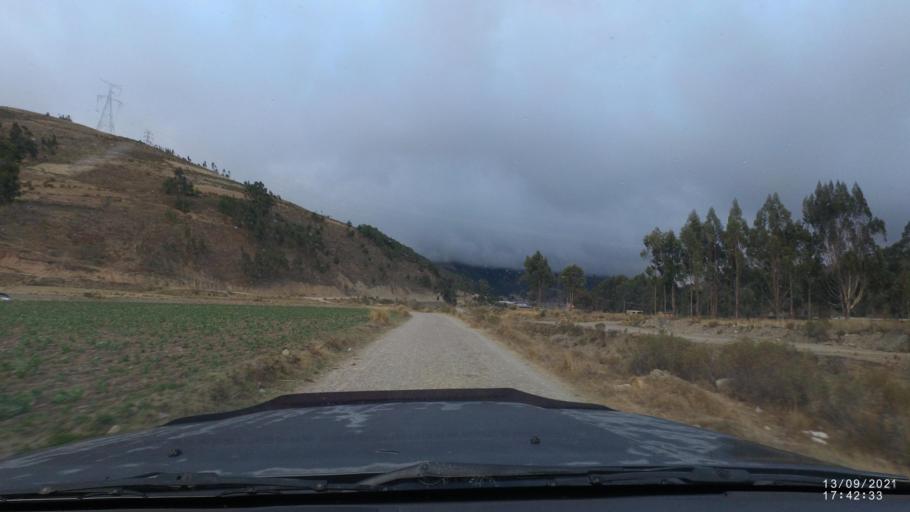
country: BO
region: Cochabamba
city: Colomi
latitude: -17.3699
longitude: -65.8175
